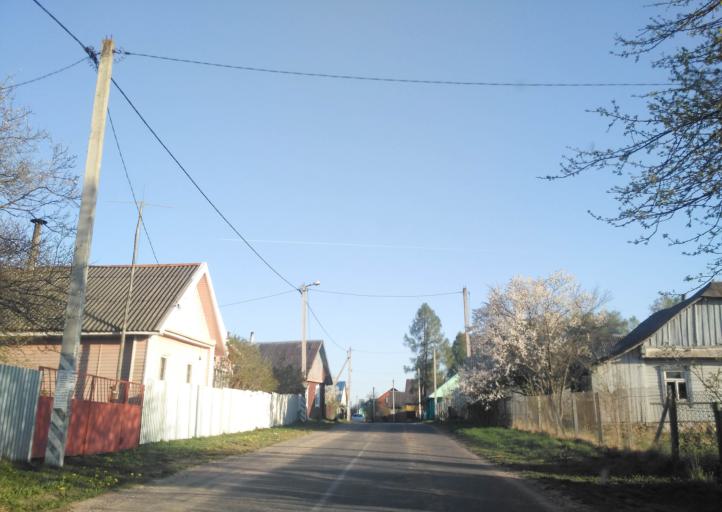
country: BY
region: Minsk
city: Pyatryshki
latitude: 54.1014
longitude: 27.1937
